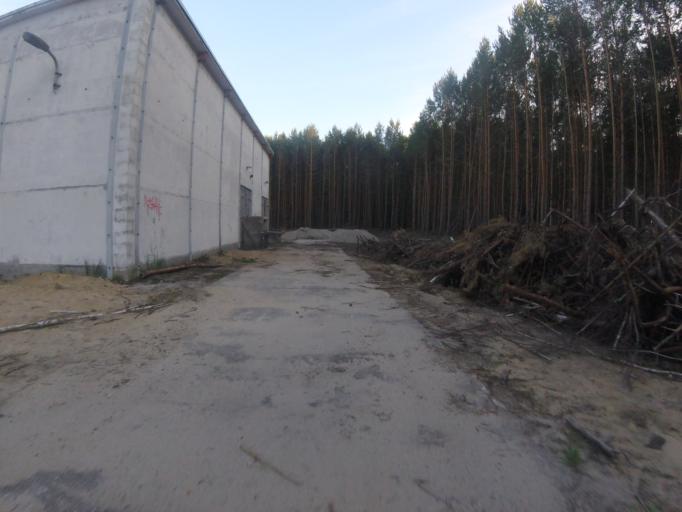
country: DE
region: Brandenburg
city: Gross Koris
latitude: 52.1804
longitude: 13.7043
